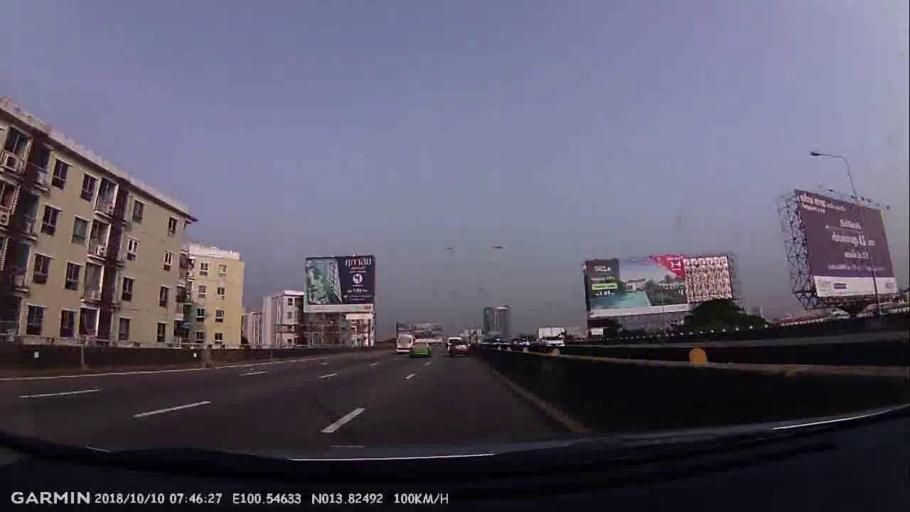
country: TH
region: Bangkok
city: Chatuchak
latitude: 13.8249
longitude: 100.5465
